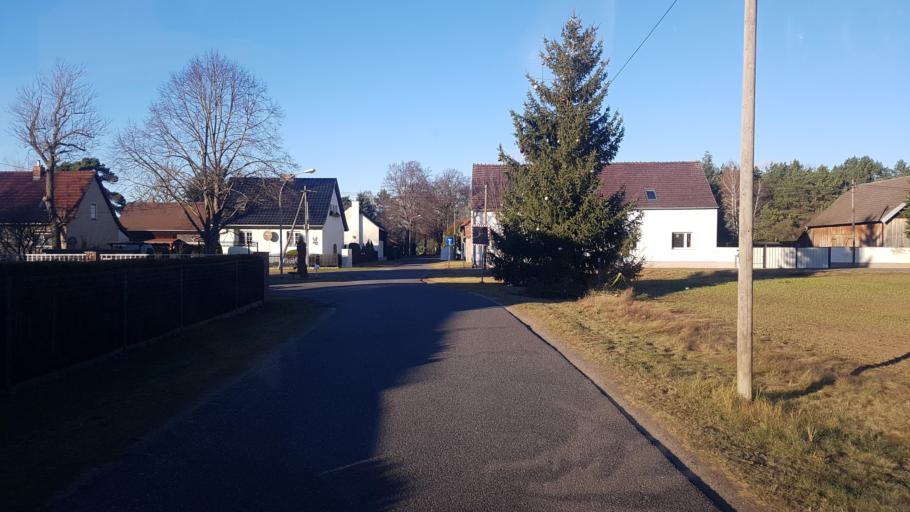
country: DE
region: Brandenburg
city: Tauer
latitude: 51.9410
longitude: 14.4542
